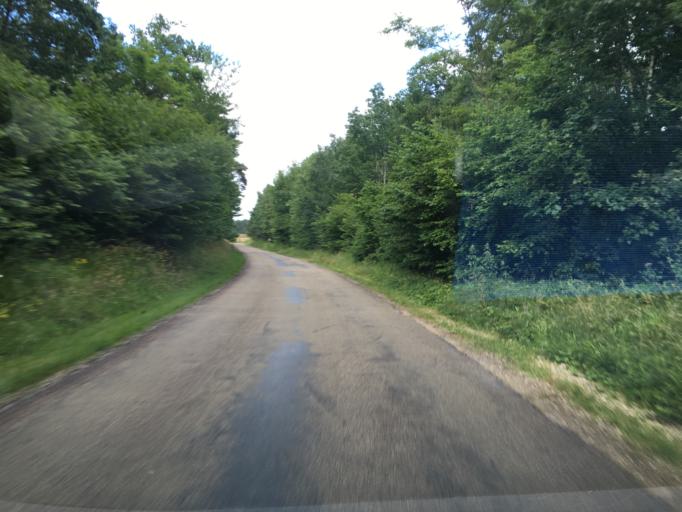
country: FR
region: Bourgogne
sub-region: Departement de l'Yonne
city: Charbuy
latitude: 47.8456
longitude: 3.4926
